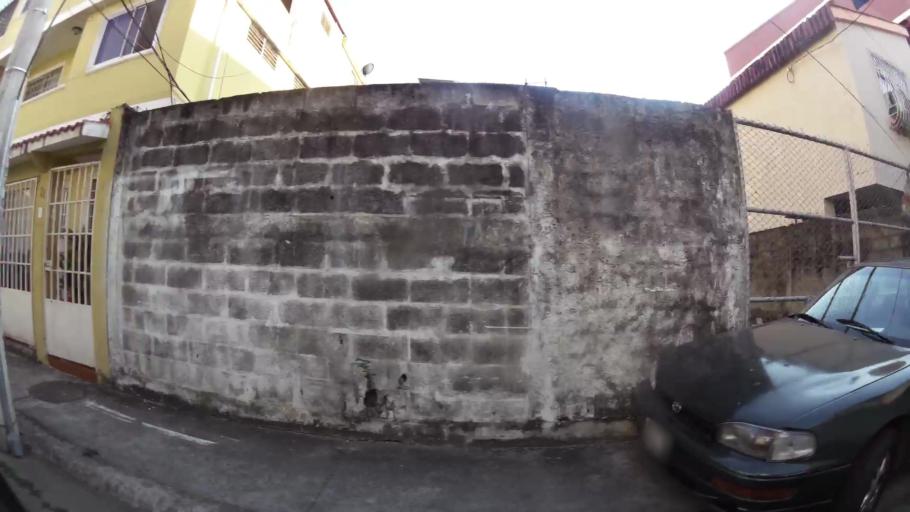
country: EC
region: Guayas
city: Guayaquil
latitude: -2.1696
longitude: -79.8961
